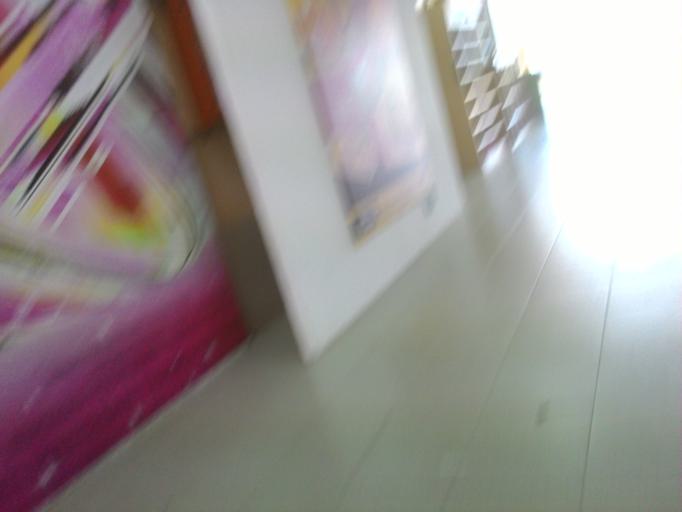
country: MY
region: Kedah
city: Kulim
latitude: 5.3837
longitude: 100.5783
